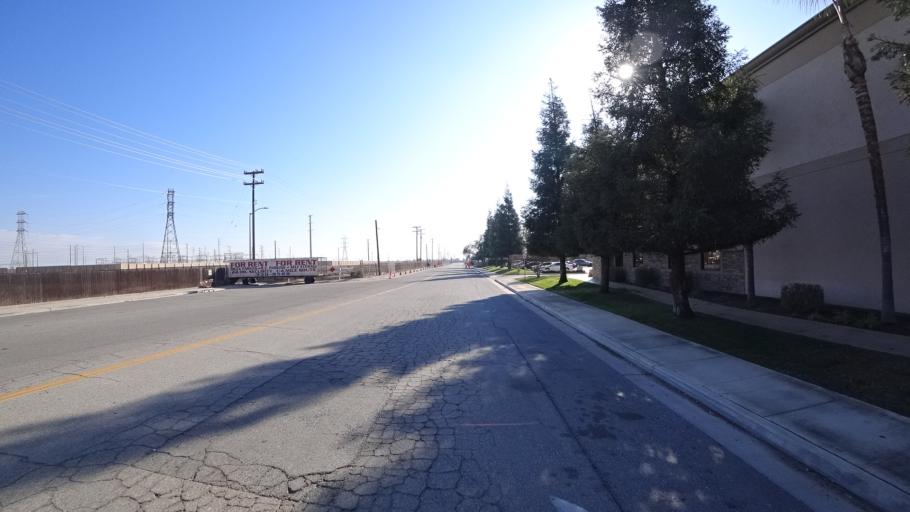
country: US
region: California
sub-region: Kern County
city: Greenacres
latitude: 35.3825
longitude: -119.1011
